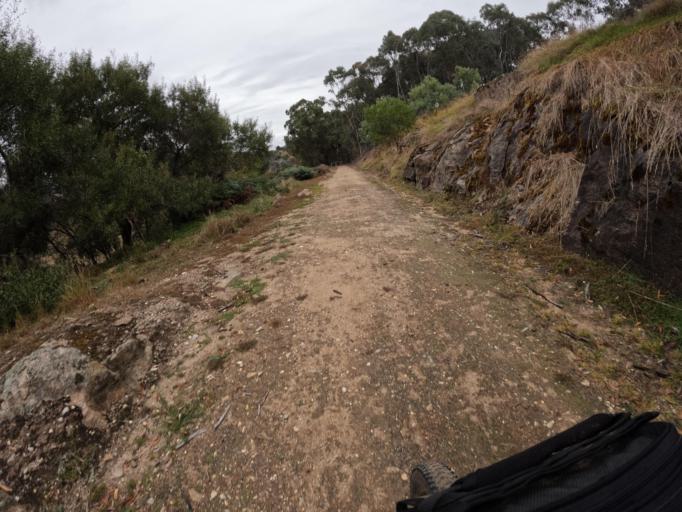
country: AU
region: New South Wales
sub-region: Greater Hume Shire
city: Holbrook
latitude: -36.1778
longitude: 147.3817
